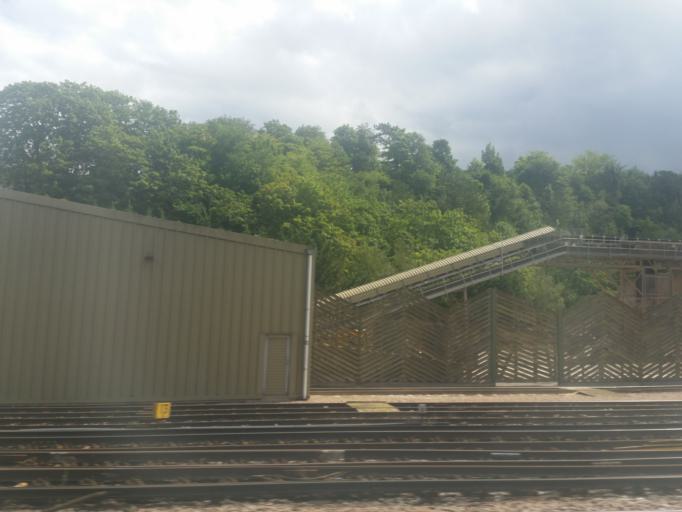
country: GB
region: England
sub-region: Greater London
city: Purley
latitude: 51.3386
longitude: -0.1121
